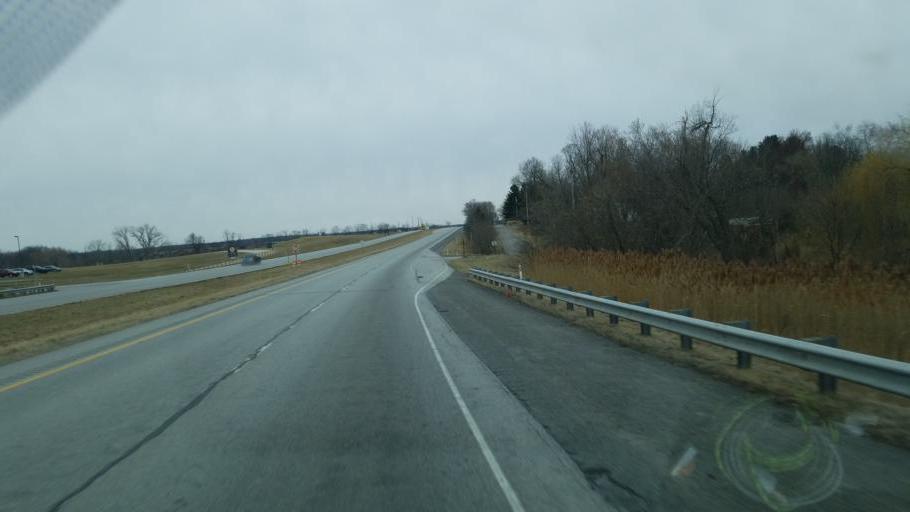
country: US
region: Indiana
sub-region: Porter County
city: Chesterton
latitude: 41.5871
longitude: -87.0445
